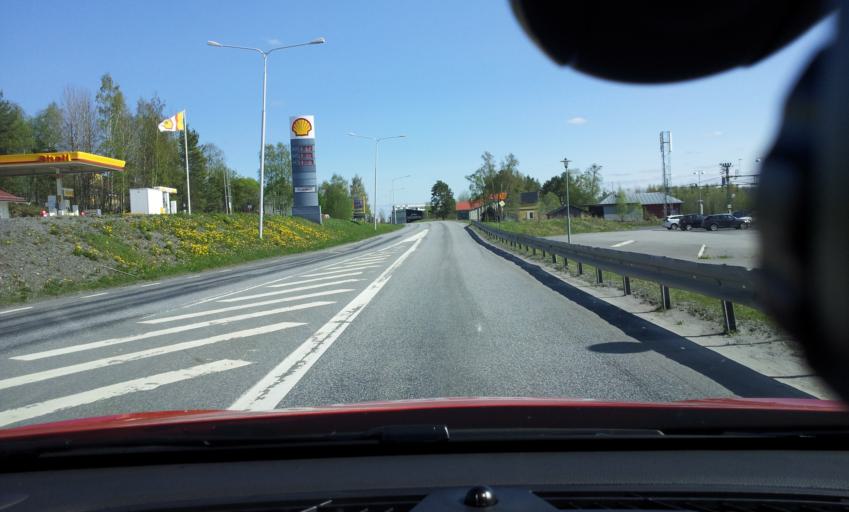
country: SE
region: Jaemtland
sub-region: Are Kommun
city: Jarpen
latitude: 63.3430
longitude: 13.4720
